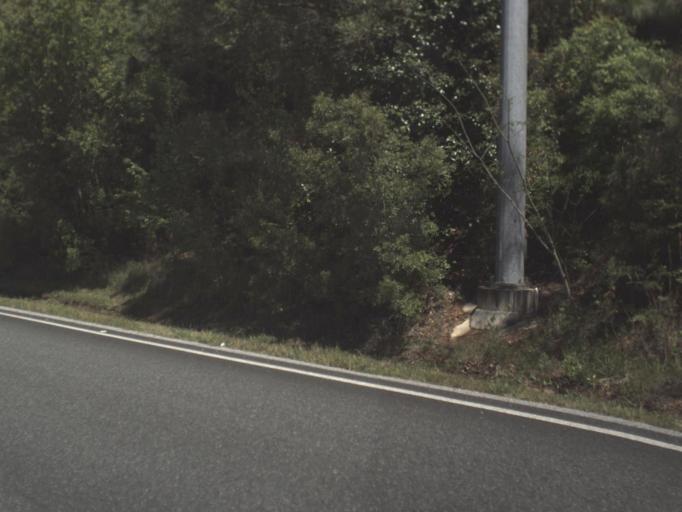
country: US
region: Florida
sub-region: Escambia County
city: Gonzalez
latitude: 30.5361
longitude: -87.3366
